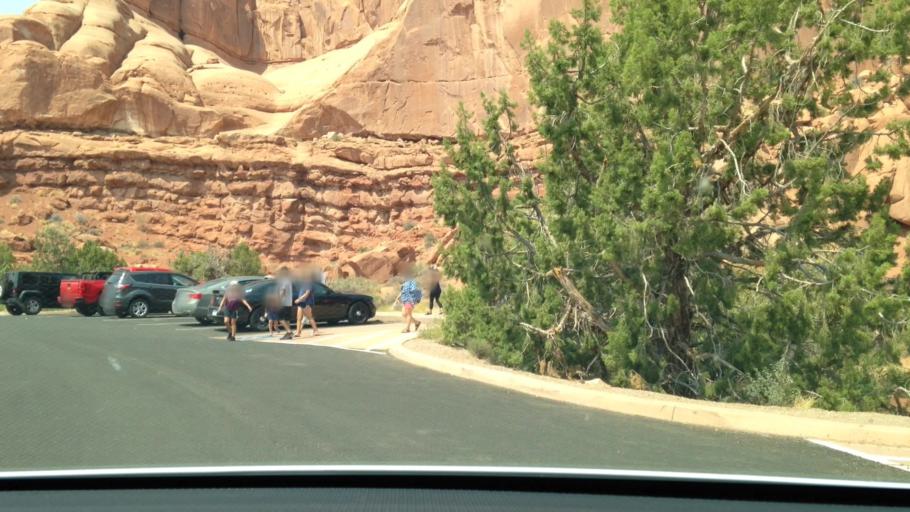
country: US
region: Utah
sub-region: Grand County
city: Moab
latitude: 38.6244
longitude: -109.5995
